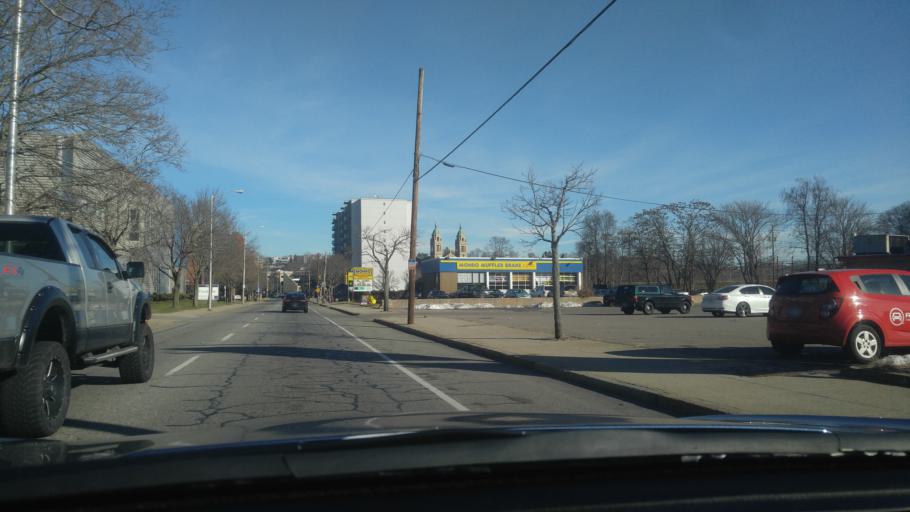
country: US
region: Rhode Island
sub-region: Providence County
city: Woonsocket
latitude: 42.0065
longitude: -71.5072
